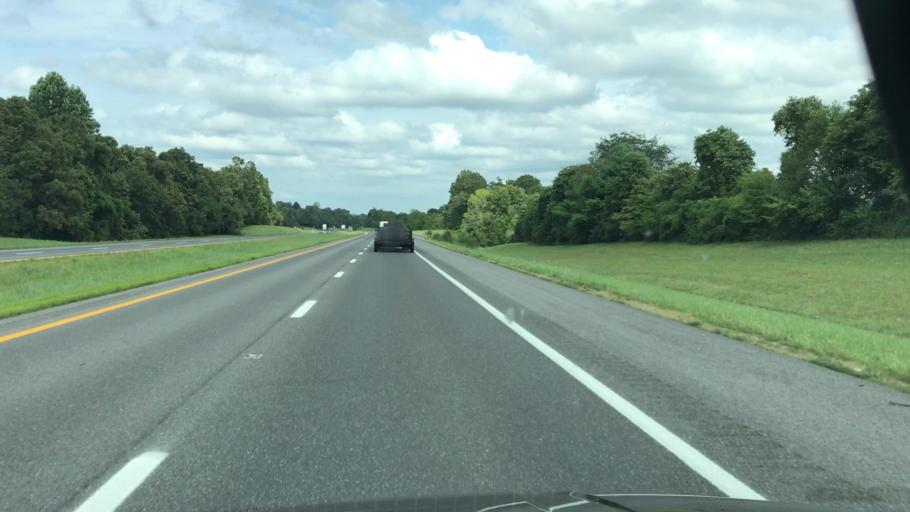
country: US
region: Kentucky
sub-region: Caldwell County
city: Princeton
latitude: 37.1142
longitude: -87.9308
